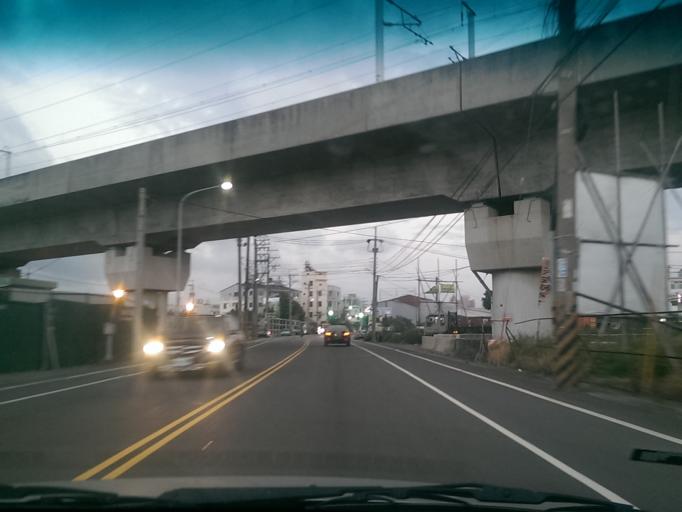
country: TW
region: Taiwan
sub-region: Taichung City
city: Taichung
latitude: 24.2178
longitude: 120.6378
